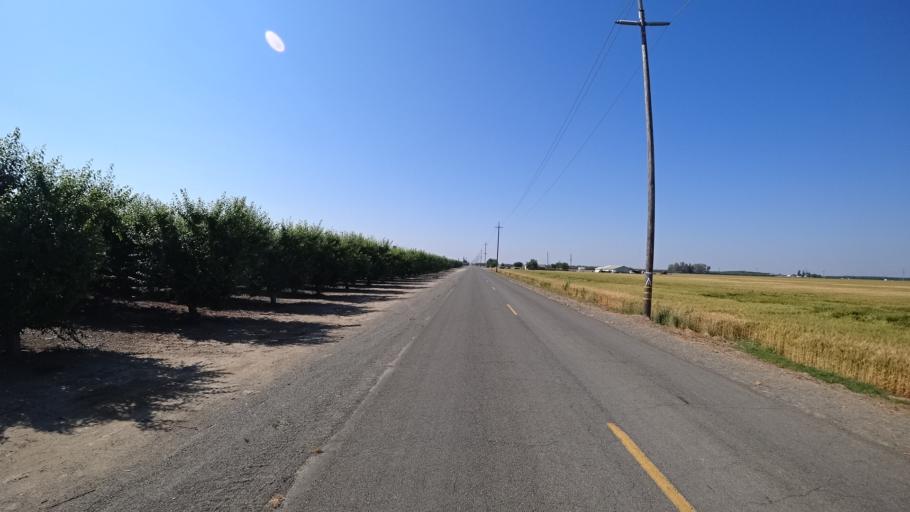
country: US
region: California
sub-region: Kings County
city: Lucerne
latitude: 36.3934
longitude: -119.5830
